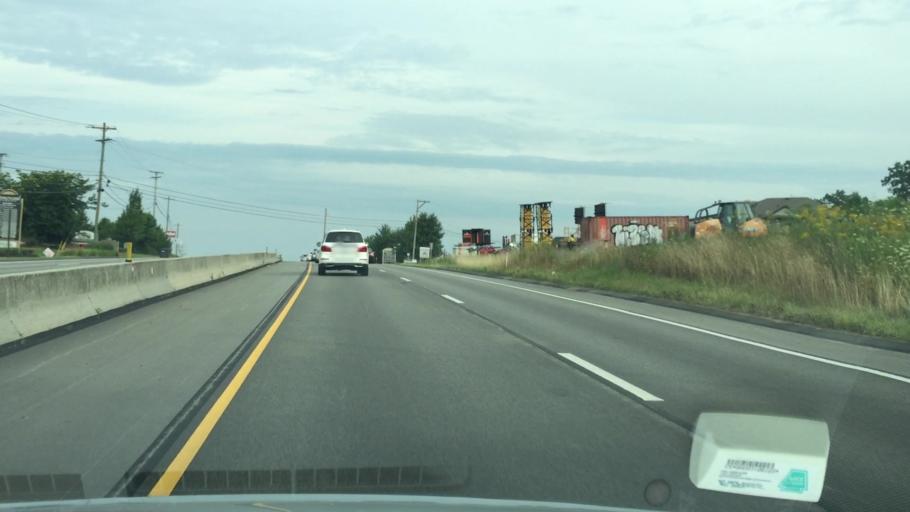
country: US
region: Pennsylvania
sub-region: Allegheny County
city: Bradford Woods
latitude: 40.6439
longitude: -80.0689
